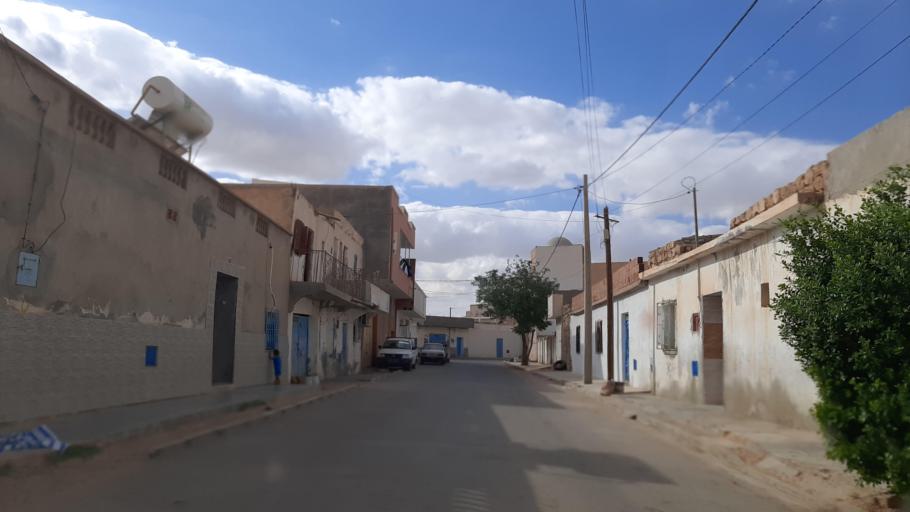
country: TN
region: Tataouine
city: Tataouine
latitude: 32.9283
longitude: 10.4562
